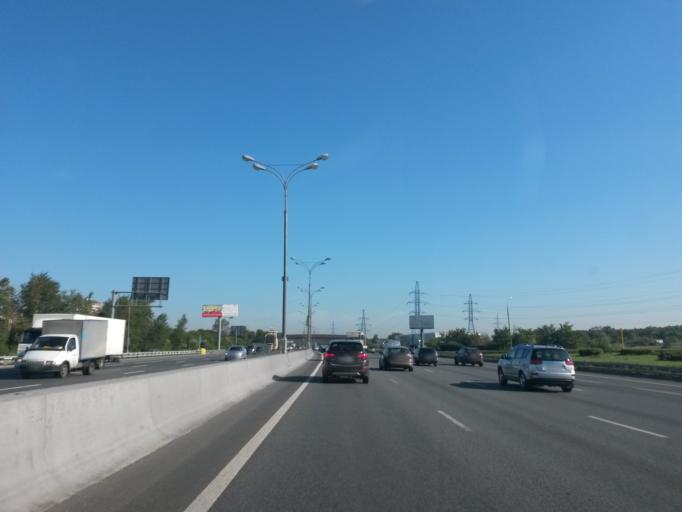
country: RU
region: Moscow
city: Gol'yanovo
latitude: 55.8148
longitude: 37.8388
